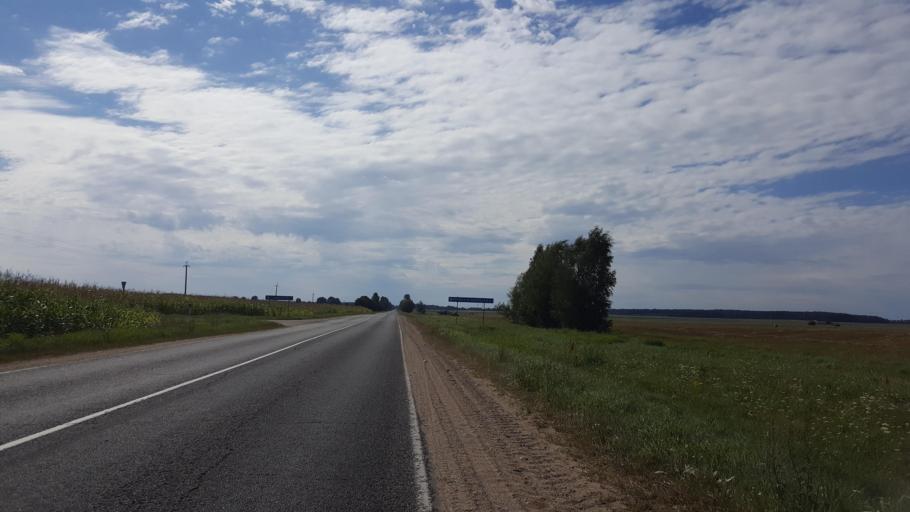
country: BY
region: Brest
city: Kamyanyets
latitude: 52.3691
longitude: 23.8850
